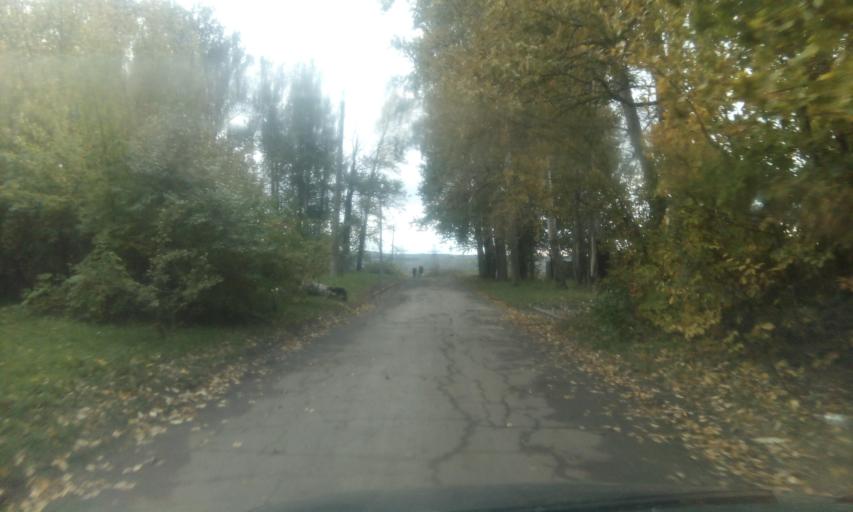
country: RU
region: Tula
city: Gritsovskiy
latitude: 54.1339
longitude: 38.1562
